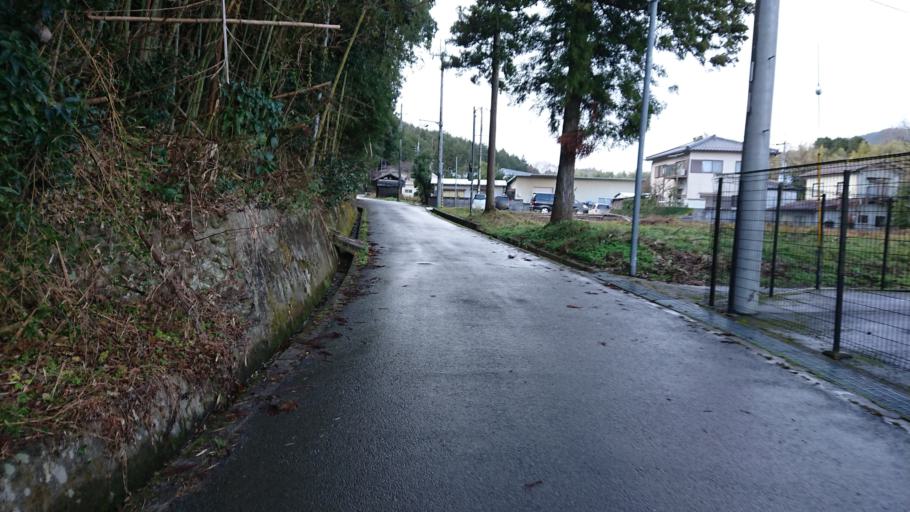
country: JP
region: Kyoto
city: Kameoka
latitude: 35.0505
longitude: 135.5123
